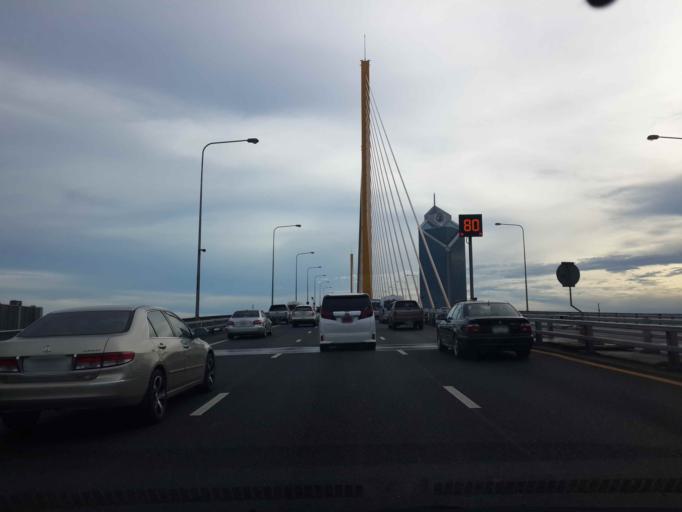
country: TH
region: Bangkok
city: Rat Burana
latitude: 13.6854
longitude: 100.5201
